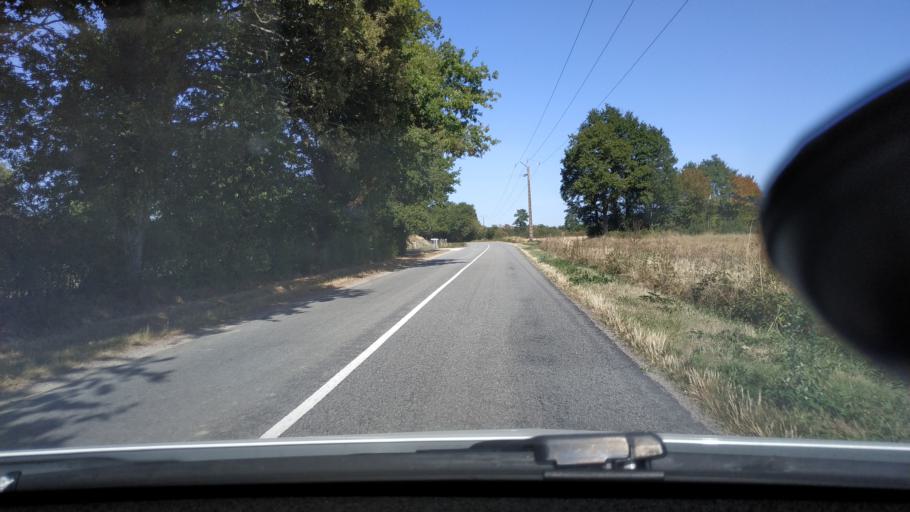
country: FR
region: Centre
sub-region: Departement du Loiret
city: Coullons
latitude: 47.6330
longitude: 2.5142
